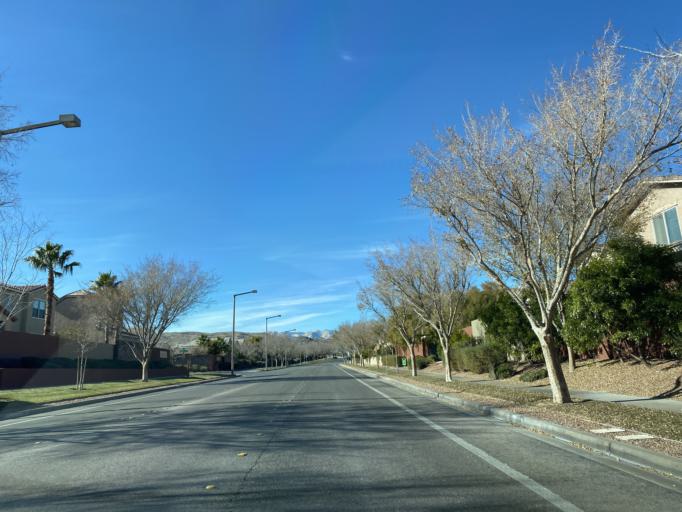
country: US
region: Nevada
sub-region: Clark County
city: Summerlin South
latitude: 36.1467
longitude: -115.3224
